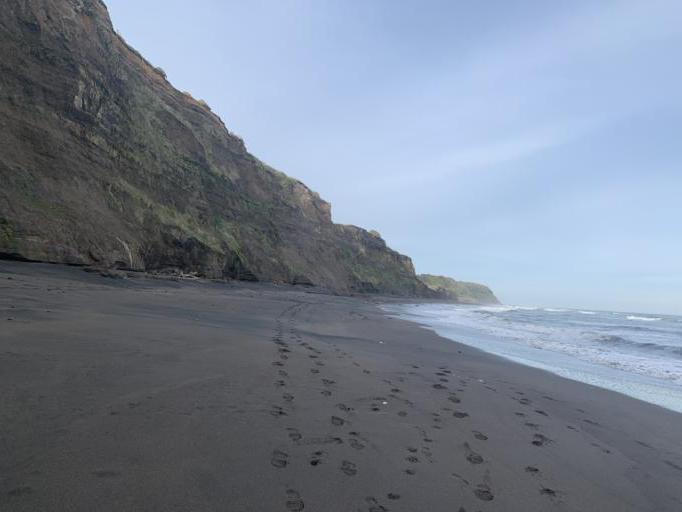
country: NZ
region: Taranaki
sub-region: South Taranaki District
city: Opunake
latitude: -39.5631
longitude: 174.0522
